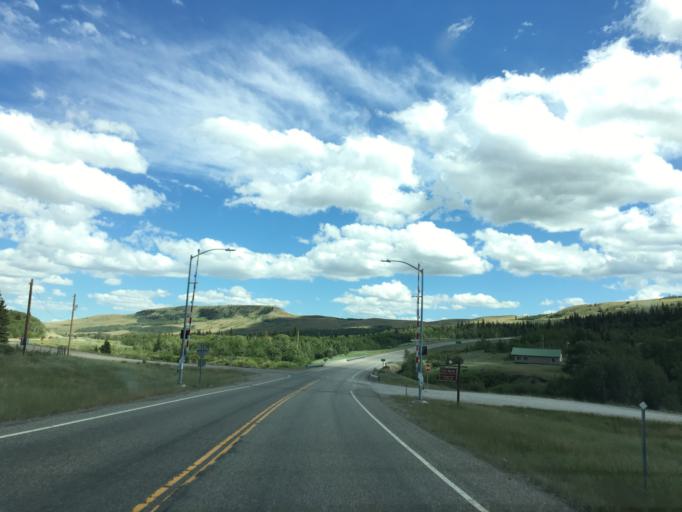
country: US
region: Montana
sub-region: Glacier County
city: Browning
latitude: 48.6097
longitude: -113.2884
